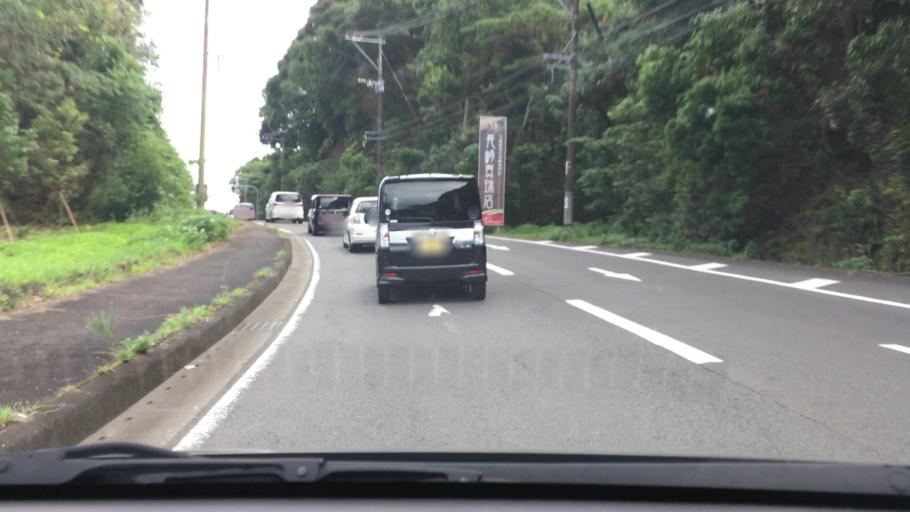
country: JP
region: Nagasaki
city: Togitsu
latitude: 32.9258
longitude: 129.7866
